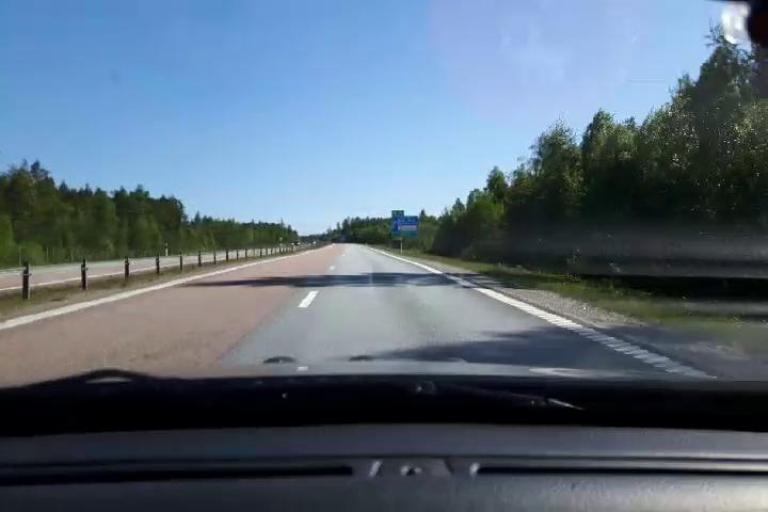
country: SE
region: Gaevleborg
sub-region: Hudiksvalls Kommun
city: Iggesund
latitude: 61.5276
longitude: 16.9720
